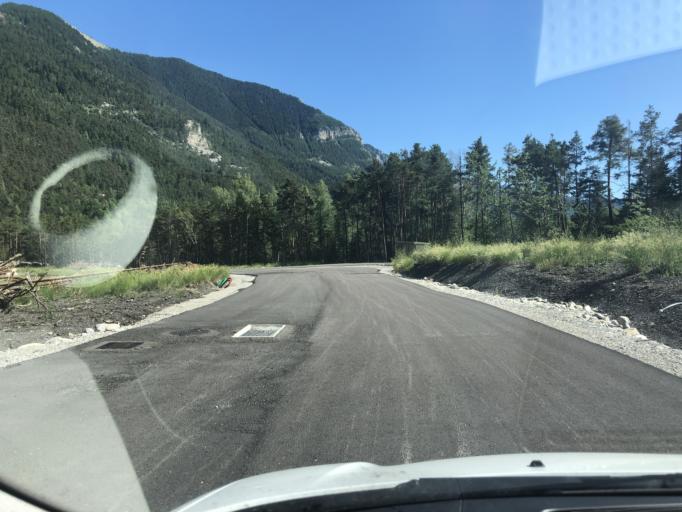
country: FR
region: Provence-Alpes-Cote d'Azur
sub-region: Departement des Alpes-de-Haute-Provence
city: Annot
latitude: 44.1580
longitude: 6.5991
